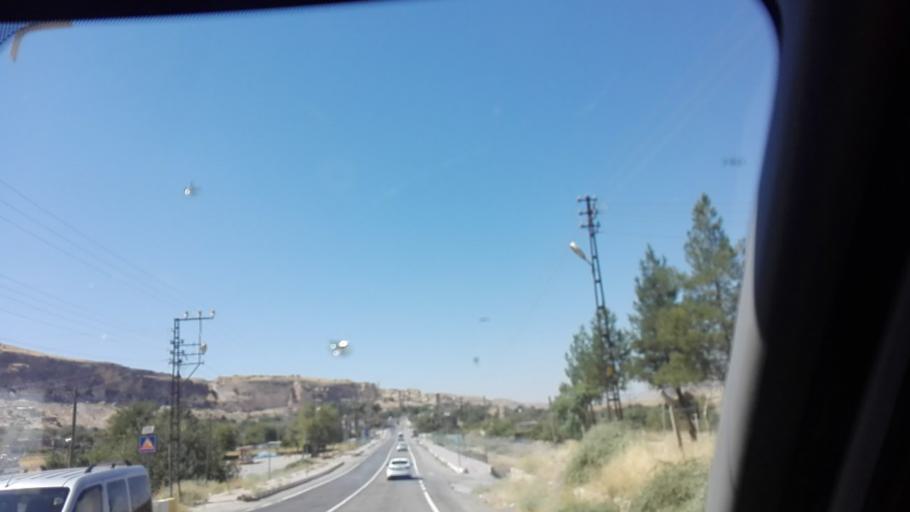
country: TR
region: Batman
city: Hasankeyf
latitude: 37.7135
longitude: 41.4246
